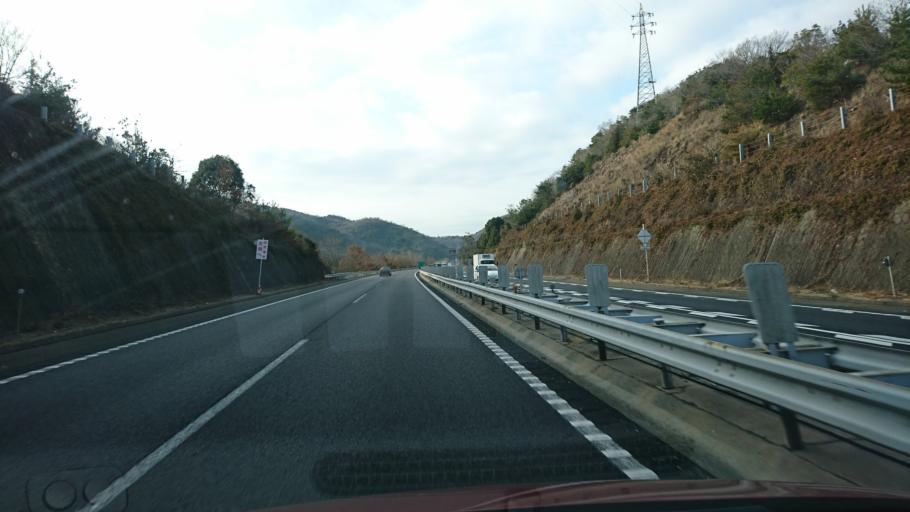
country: JP
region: Hyogo
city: Aioi
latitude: 34.7993
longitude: 134.4354
